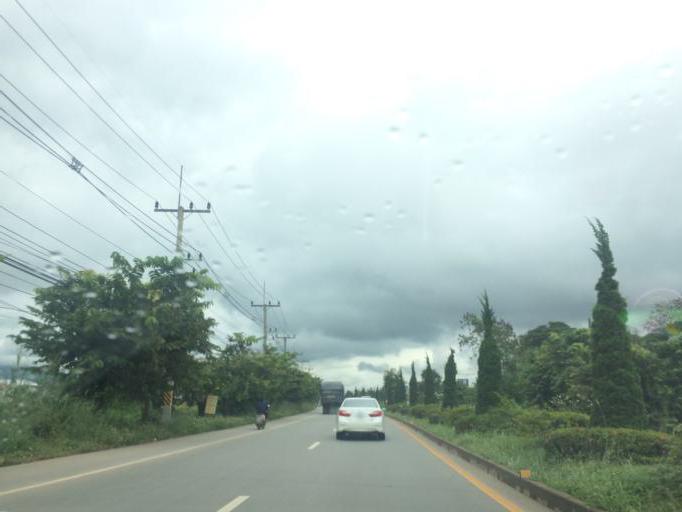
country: TH
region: Chiang Rai
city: Mae Chan
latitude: 20.0284
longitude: 99.8732
